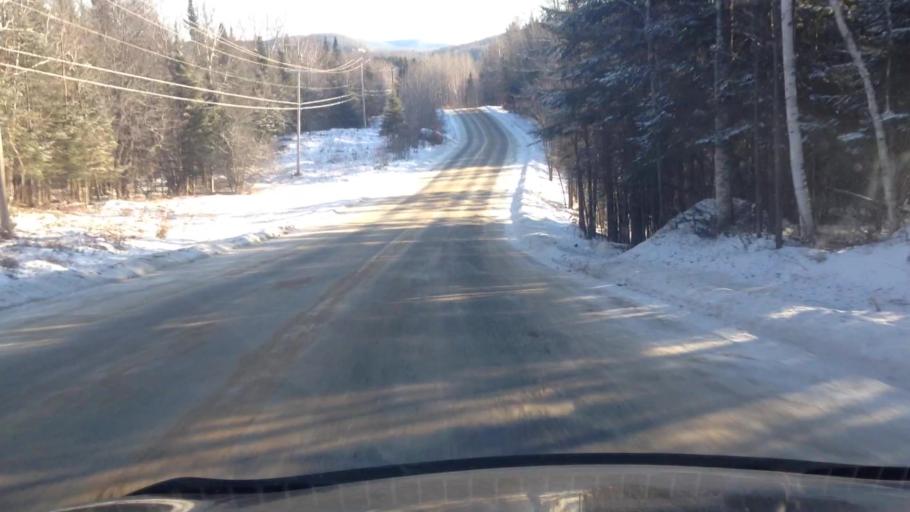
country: CA
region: Quebec
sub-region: Laurentides
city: Brownsburg-Chatham
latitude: 45.9234
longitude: -74.5375
